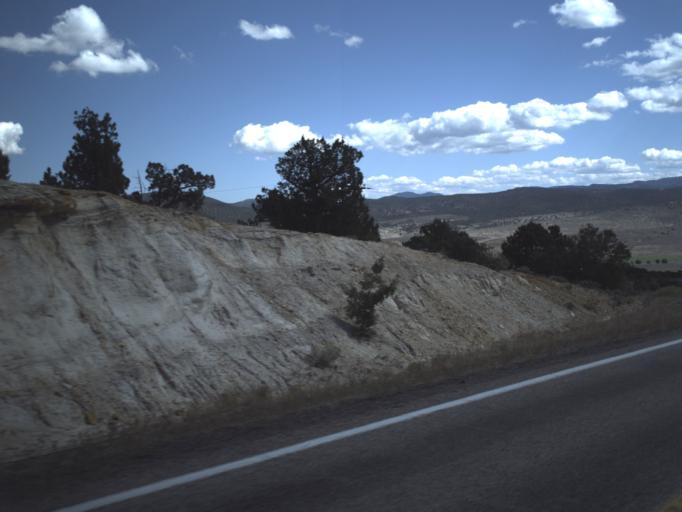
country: US
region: Utah
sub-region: Washington County
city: Enterprise
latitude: 37.5260
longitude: -113.6444
